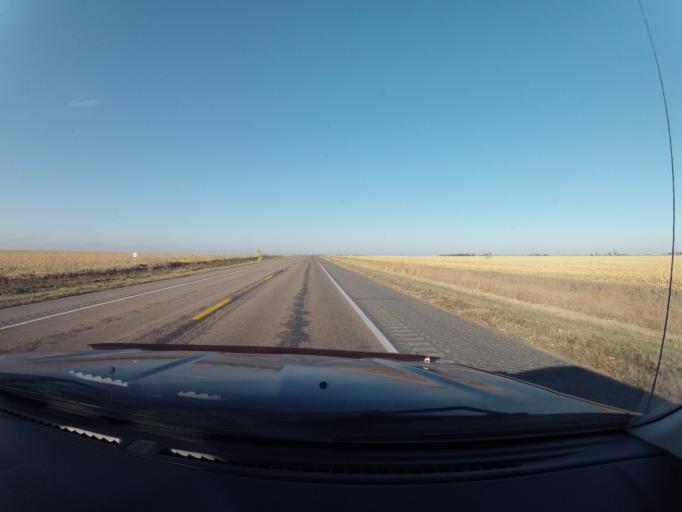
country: US
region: Nebraska
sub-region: Kearney County
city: Minden
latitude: 40.5558
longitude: -98.9518
